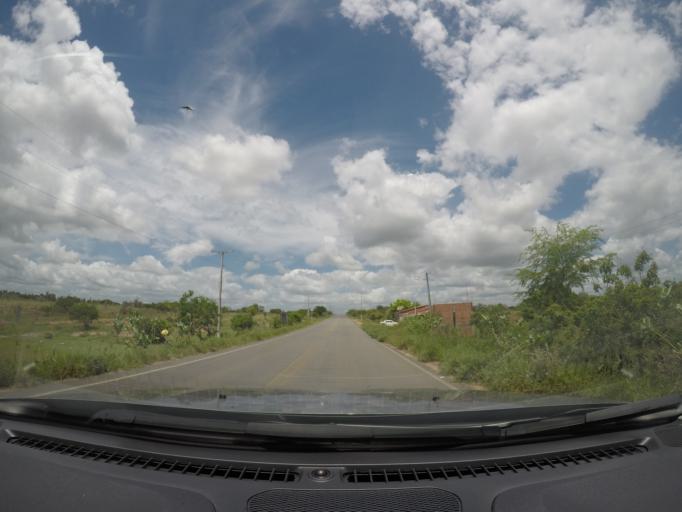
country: BR
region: Bahia
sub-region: Ipira
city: Ipira
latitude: -12.3009
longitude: -39.8934
